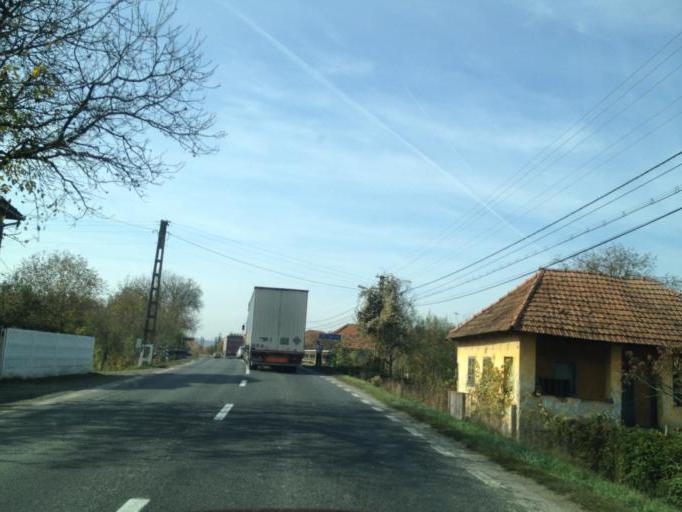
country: RO
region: Hunedoara
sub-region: Comuna Ilia
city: Ilia
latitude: 45.9160
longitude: 22.6206
